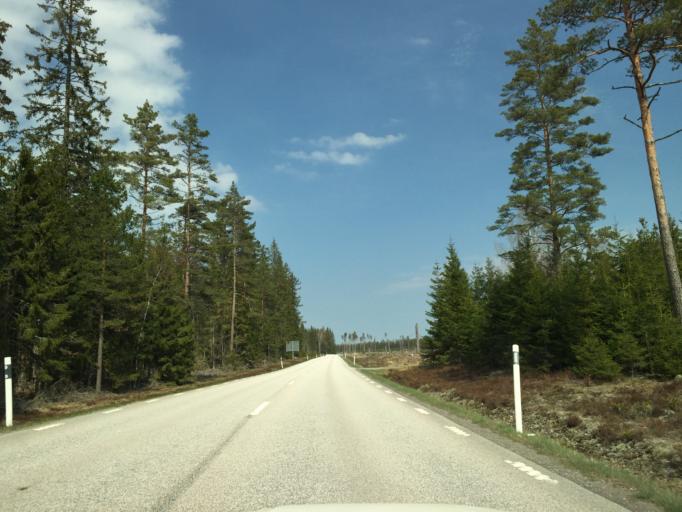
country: SE
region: Vaestra Goetaland
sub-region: Bengtsfors Kommun
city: Dals Langed
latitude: 58.8290
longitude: 12.1415
